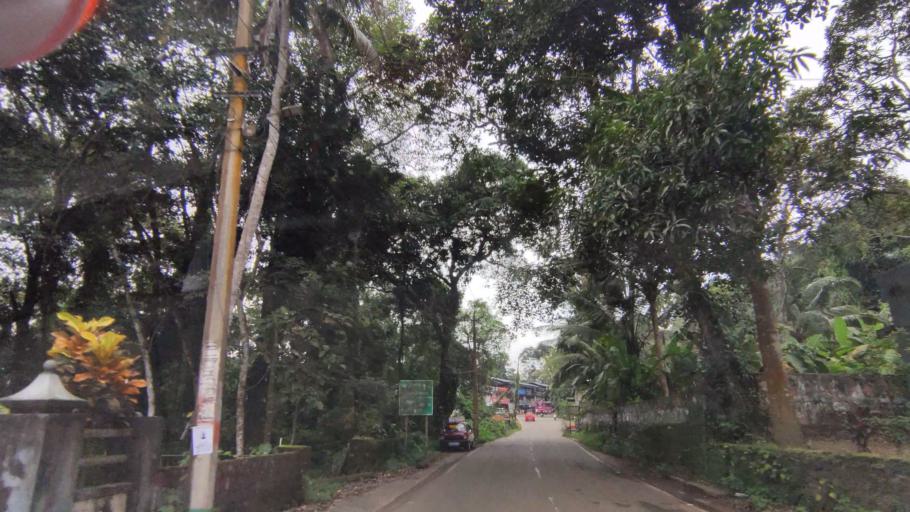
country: IN
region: Kerala
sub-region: Kottayam
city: Kottayam
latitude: 9.6586
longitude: 76.5300
